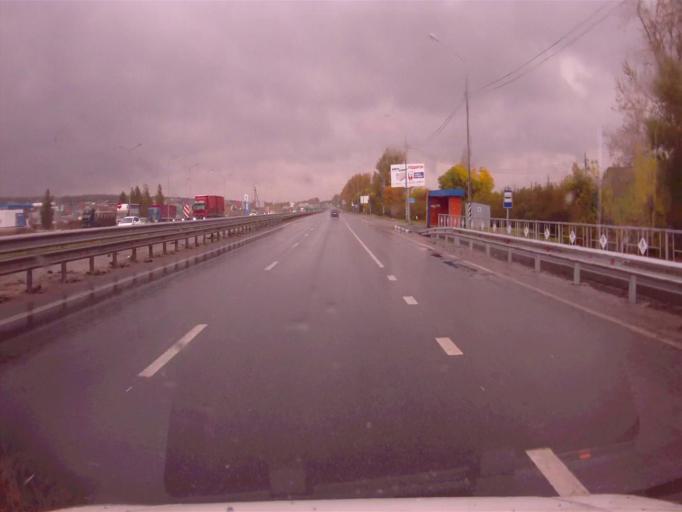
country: RU
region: Chelyabinsk
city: Dolgoderevenskoye
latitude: 55.2752
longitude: 61.3439
